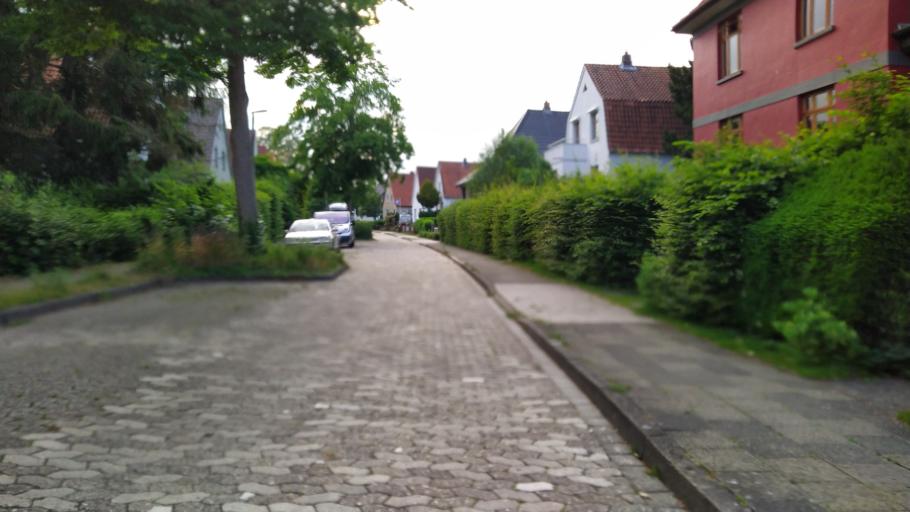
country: DE
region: Lower Saxony
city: Buxtehude
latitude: 53.4740
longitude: 9.6905
